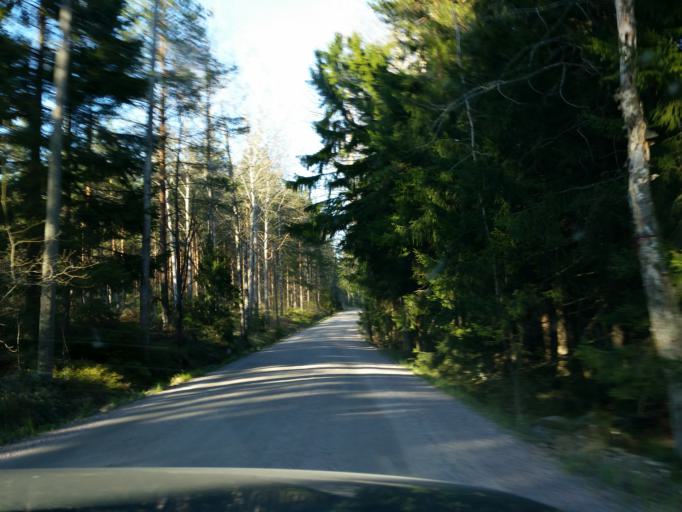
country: FI
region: Uusimaa
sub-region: Helsinki
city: Espoo
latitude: 60.1049
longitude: 24.5999
